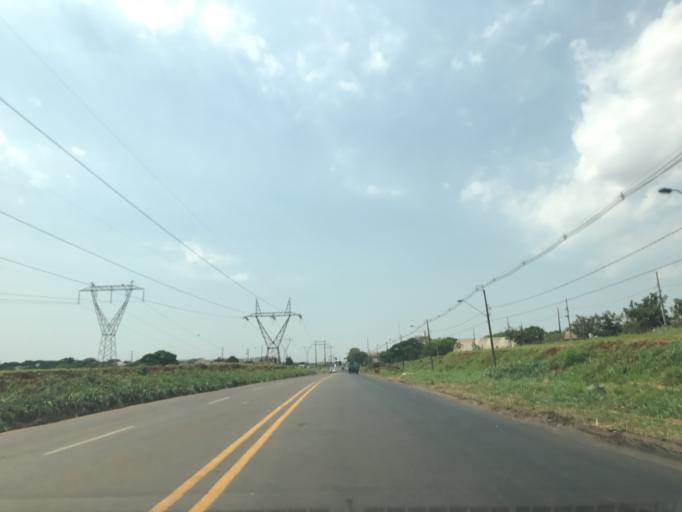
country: BR
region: Parana
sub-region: Maringa
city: Maringa
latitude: -23.4603
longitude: -51.9231
